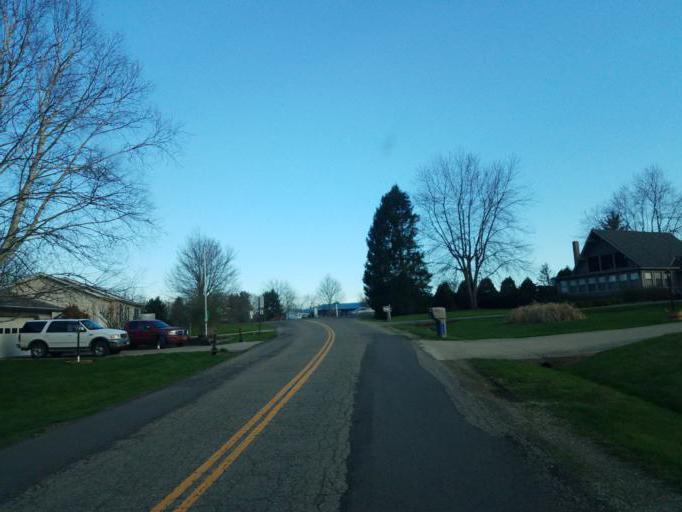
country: US
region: Ohio
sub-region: Knox County
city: Gambier
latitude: 40.4122
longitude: -82.3526
